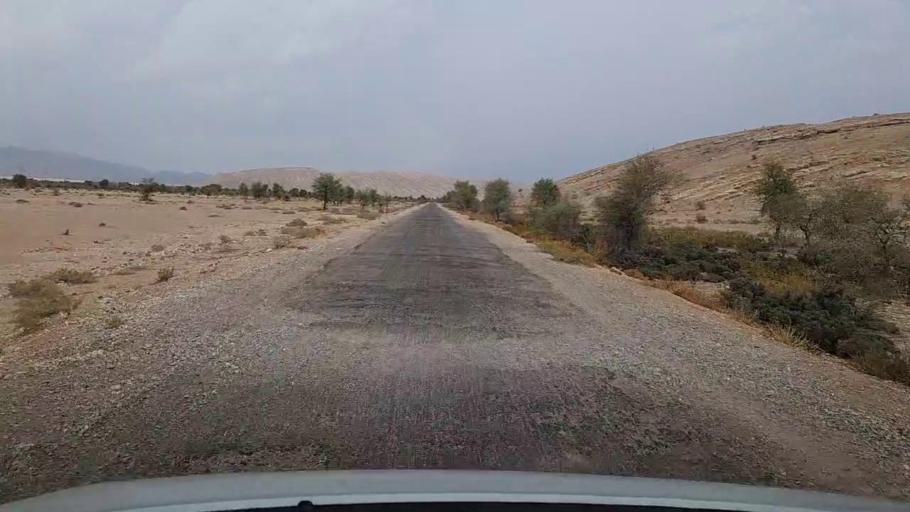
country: PK
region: Sindh
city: Sehwan
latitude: 26.2265
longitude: 67.7089
